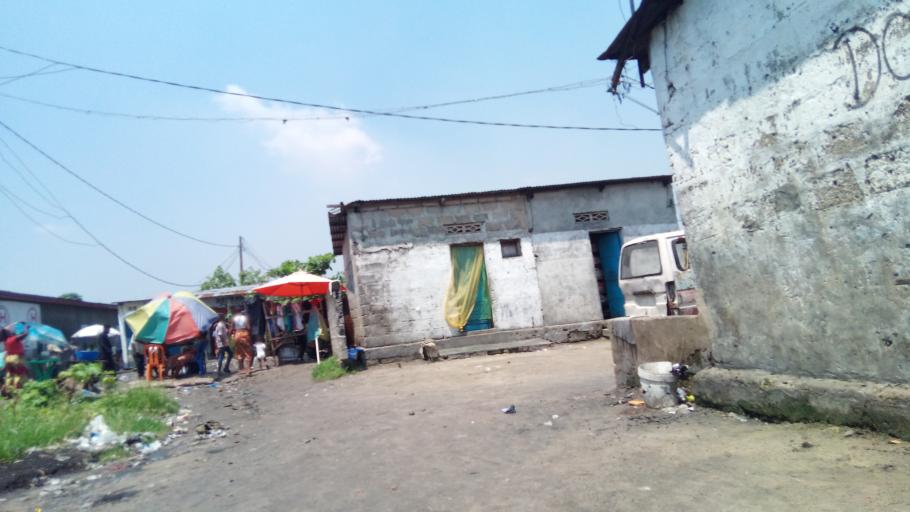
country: CD
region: Kinshasa
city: Kinshasa
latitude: -4.3681
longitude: 15.3088
